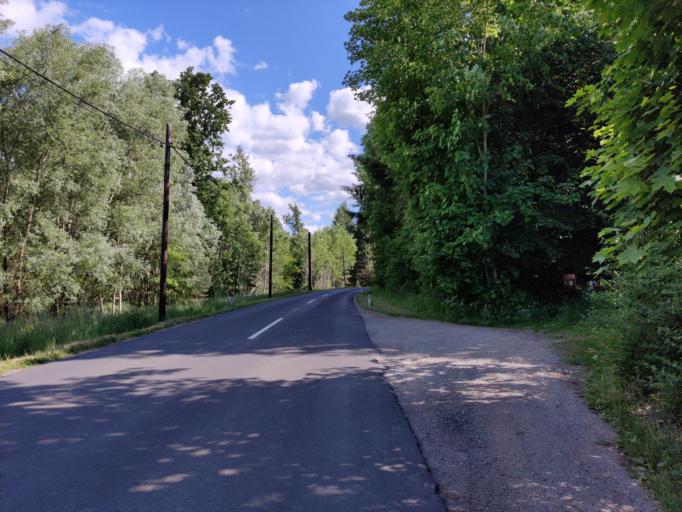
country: AT
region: Styria
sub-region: Politischer Bezirk Graz-Umgebung
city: Thal
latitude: 47.0491
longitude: 15.3616
